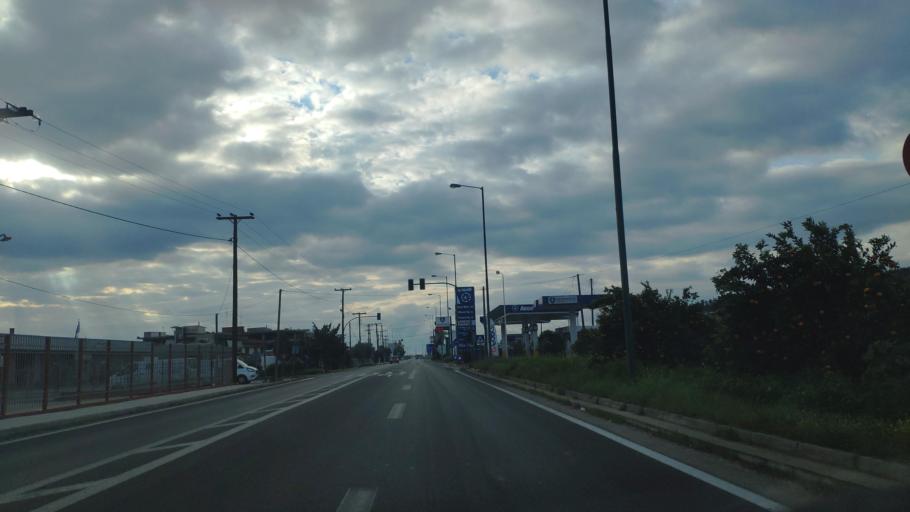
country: GR
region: Peloponnese
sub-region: Nomos Argolidos
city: Argos
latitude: 37.6527
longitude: 22.7279
